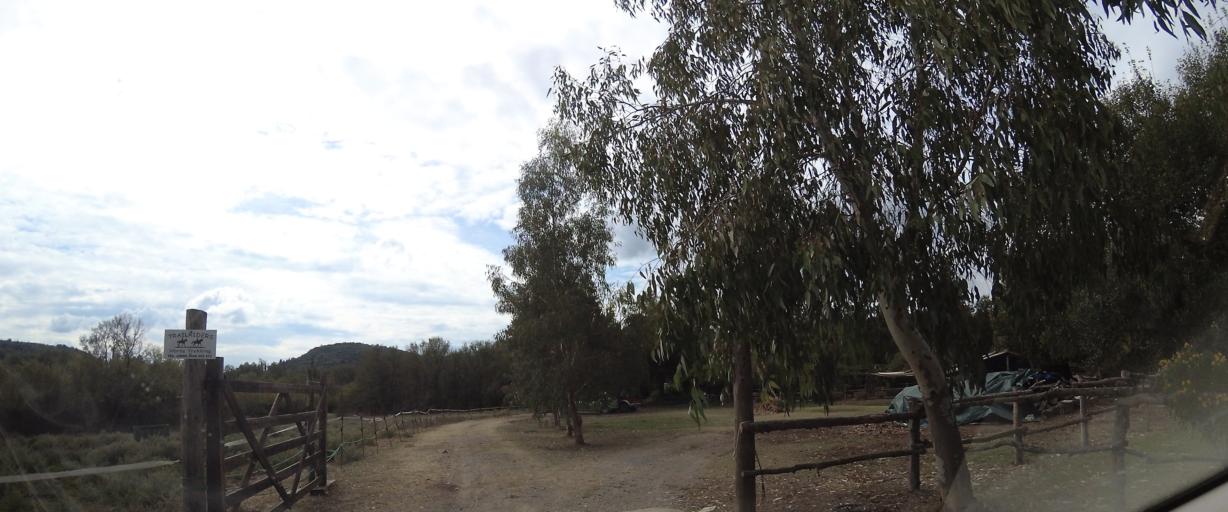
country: GR
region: Ionian Islands
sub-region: Nomos Kerkyras
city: Kontokali
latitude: 39.6973
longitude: 19.8021
